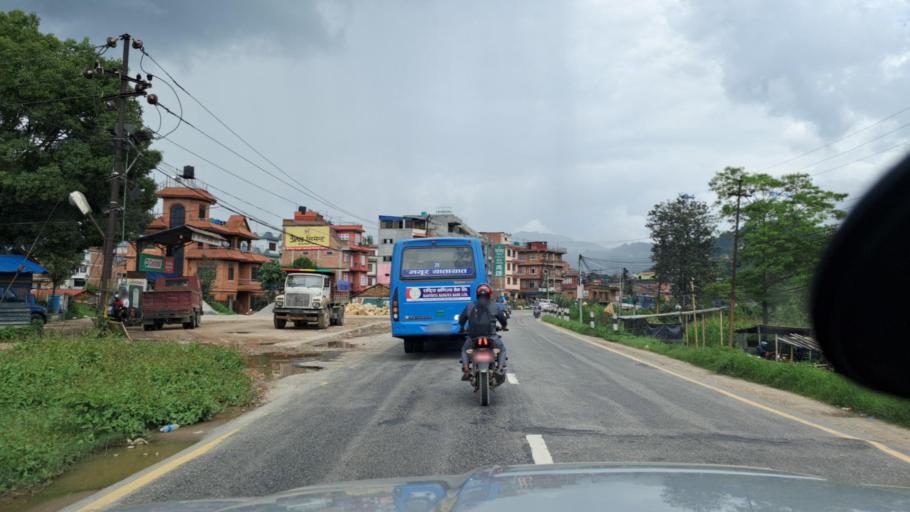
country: NP
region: Central Region
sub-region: Bagmati Zone
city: Hari Bdr Tamang House
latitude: 27.6538
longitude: 85.4585
